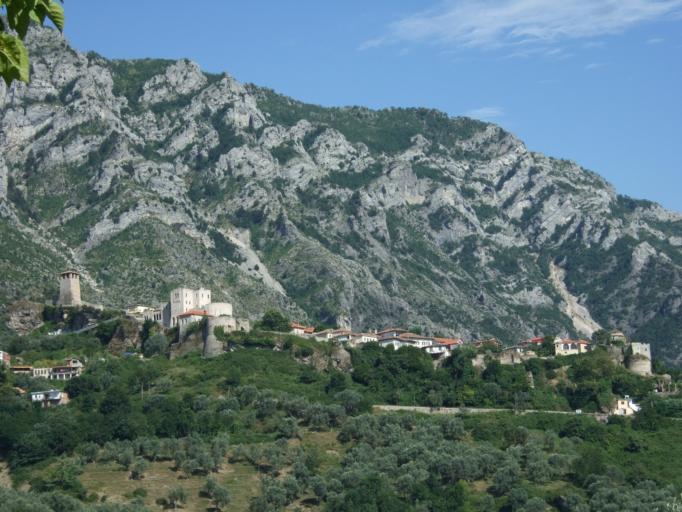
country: AL
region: Durres
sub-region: Rrethi i Krujes
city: Kruje
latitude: 41.5095
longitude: 19.7837
